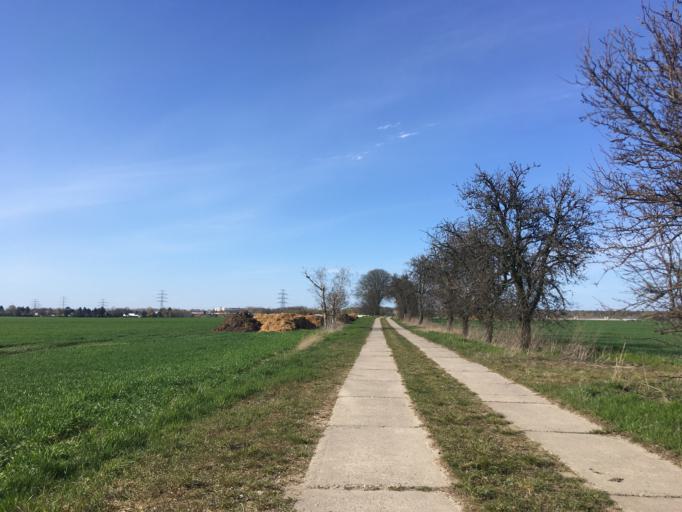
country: DE
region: Berlin
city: Buch
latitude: 52.6099
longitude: 13.5106
